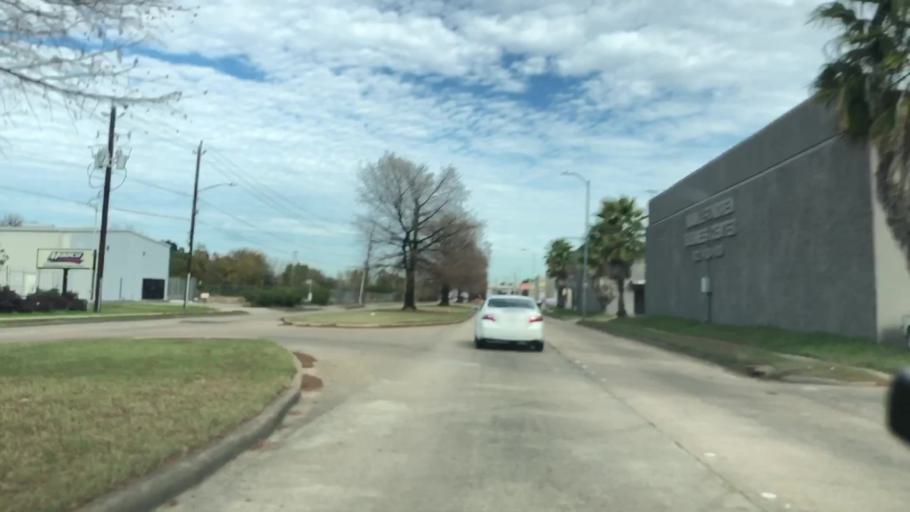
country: US
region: Texas
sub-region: Fort Bend County
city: Missouri City
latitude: 29.6263
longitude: -95.5073
